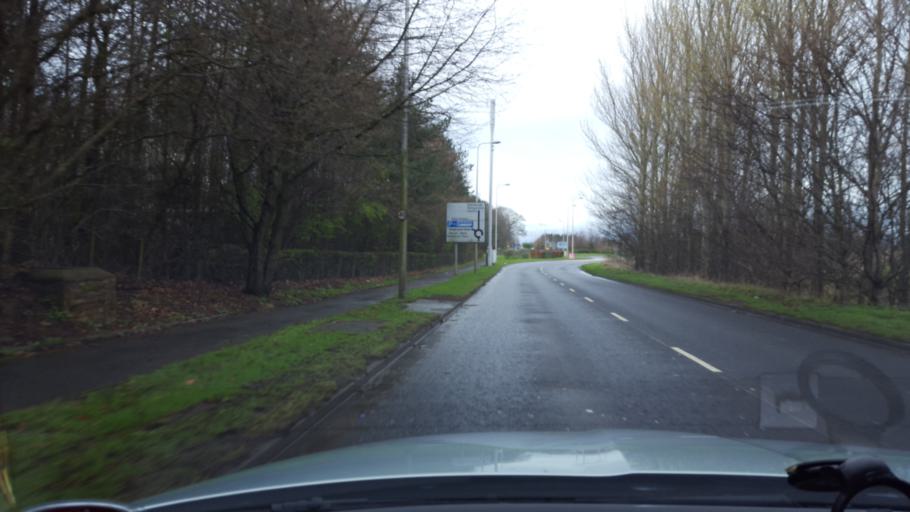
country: GB
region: Scotland
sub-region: Edinburgh
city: Currie
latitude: 55.9141
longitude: -3.3133
